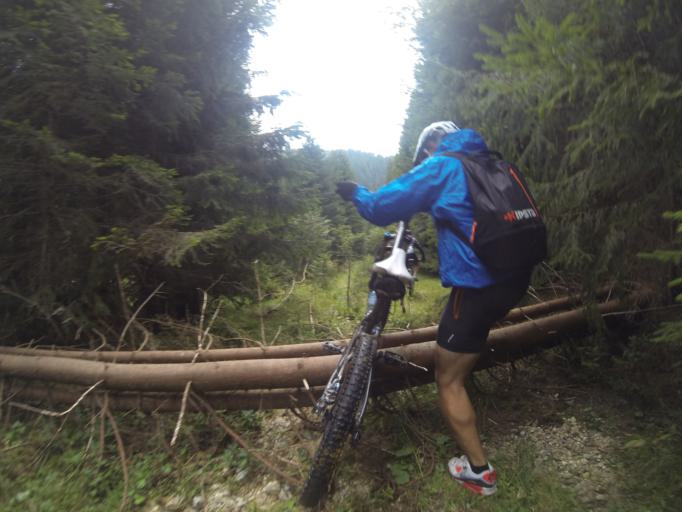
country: RO
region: Gorj
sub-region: Comuna Polovragi
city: Polovragi
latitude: 45.2805
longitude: 23.8369
